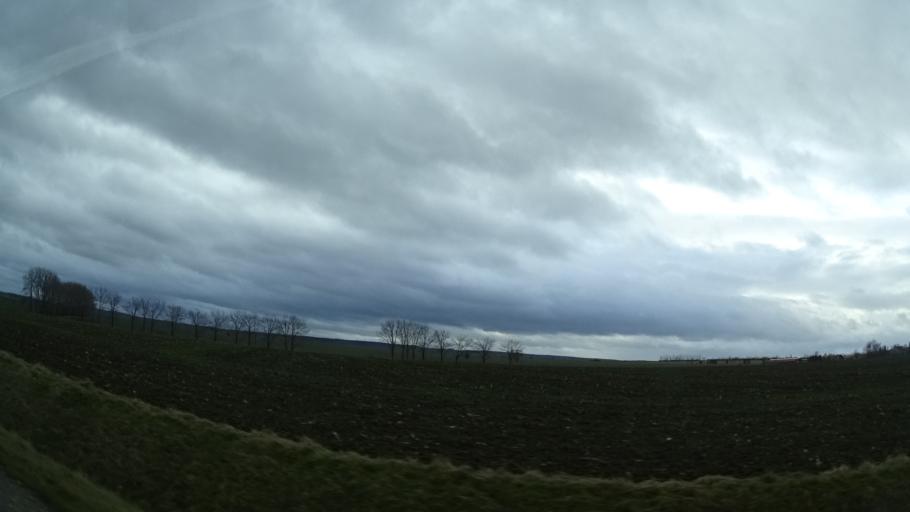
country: DE
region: Thuringia
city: Milda
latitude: 50.8420
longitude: 11.4119
